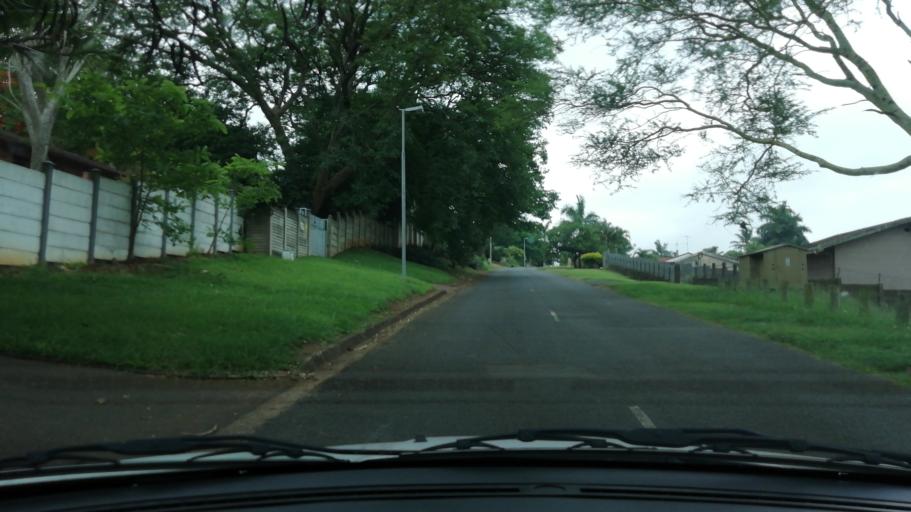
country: ZA
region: KwaZulu-Natal
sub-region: uThungulu District Municipality
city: Empangeni
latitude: -28.7383
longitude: 31.9024
